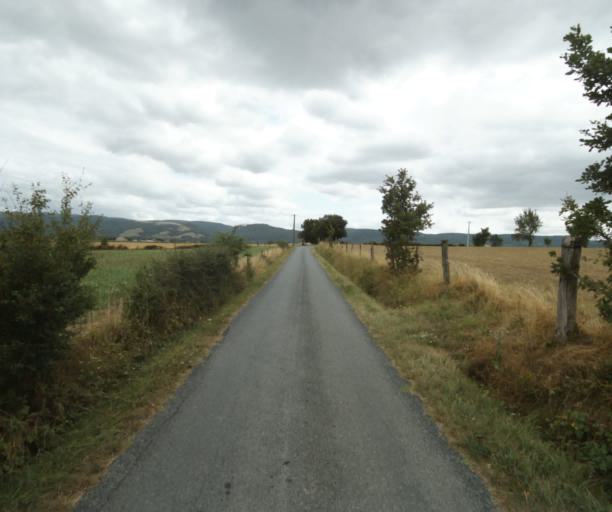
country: FR
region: Midi-Pyrenees
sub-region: Departement du Tarn
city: Soreze
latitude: 43.4774
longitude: 2.0482
